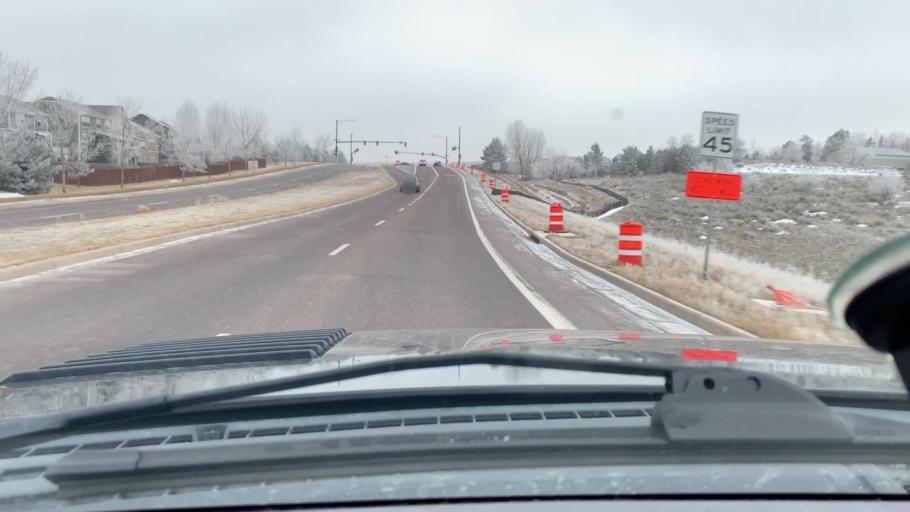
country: US
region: Colorado
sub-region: Douglas County
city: Stonegate
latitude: 39.5388
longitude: -104.8114
